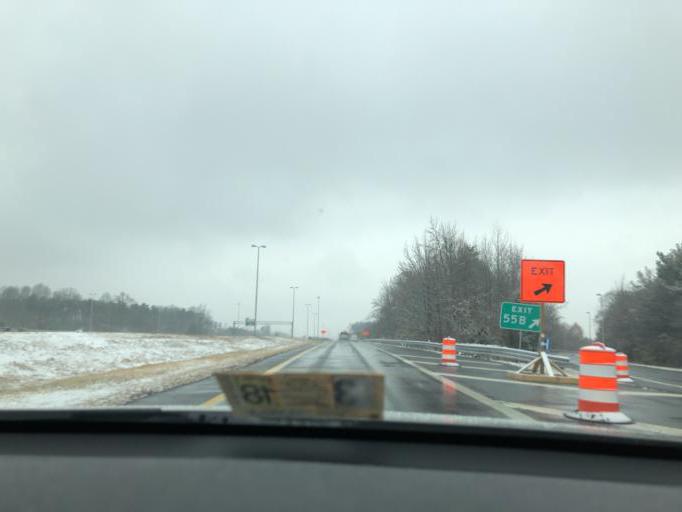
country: US
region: Virginia
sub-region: Fairfax County
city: Greenbriar
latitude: 38.8559
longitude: -77.3835
